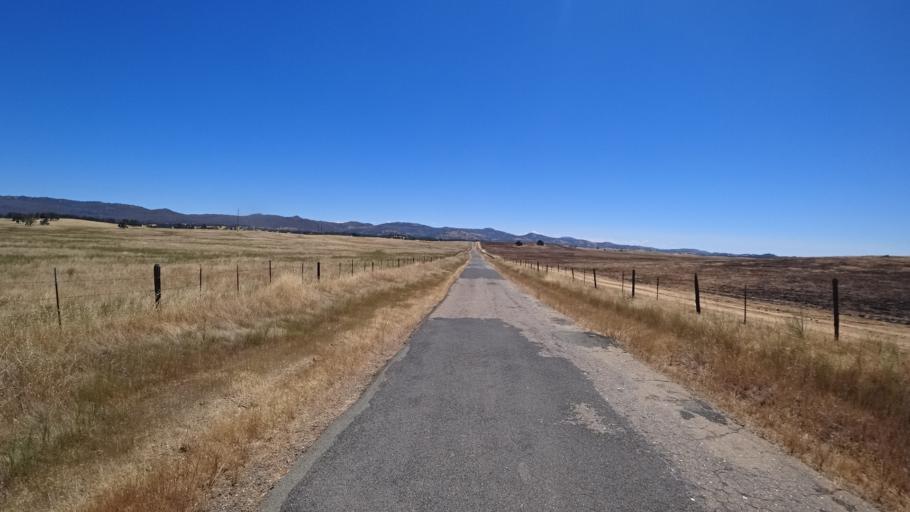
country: US
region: California
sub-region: Calaveras County
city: Rancho Calaveras
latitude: 38.0573
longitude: -120.7707
